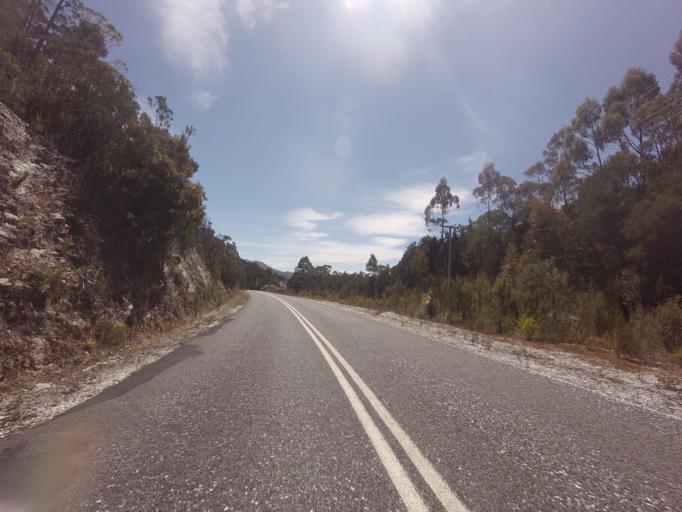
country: AU
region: Tasmania
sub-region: West Coast
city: Queenstown
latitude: -42.7611
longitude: 146.0046
